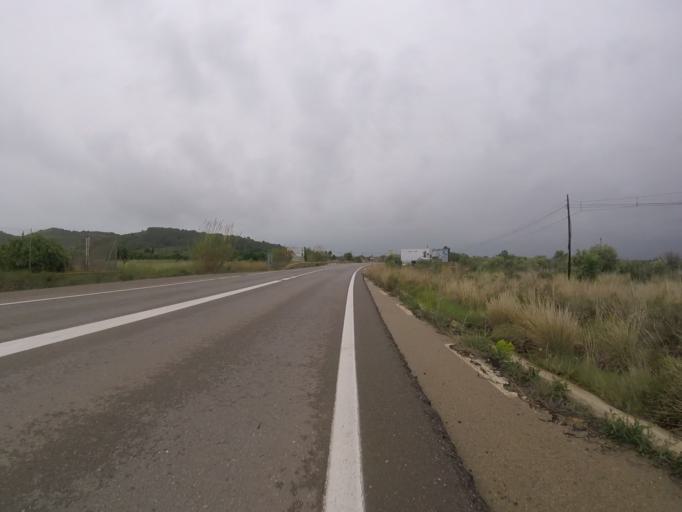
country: ES
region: Valencia
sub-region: Provincia de Castello
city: Alcoceber
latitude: 40.2551
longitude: 0.2454
